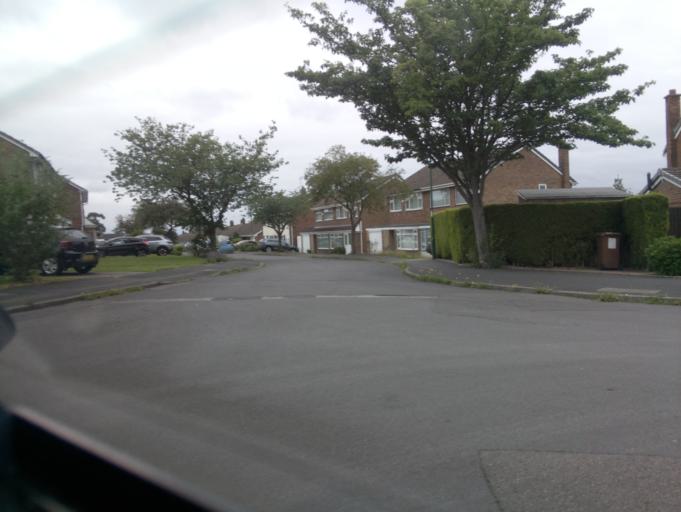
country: GB
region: England
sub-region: Nottinghamshire
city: Arnold
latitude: 52.9830
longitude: -1.1303
